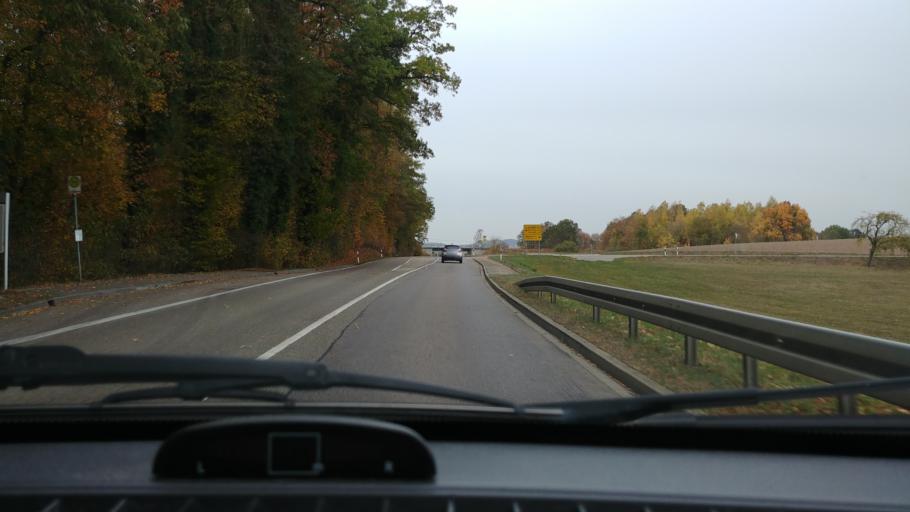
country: DE
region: Baden-Wuerttemberg
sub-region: Regierungsbezirk Stuttgart
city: Wallhausen
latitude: 49.2274
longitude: 10.0505
